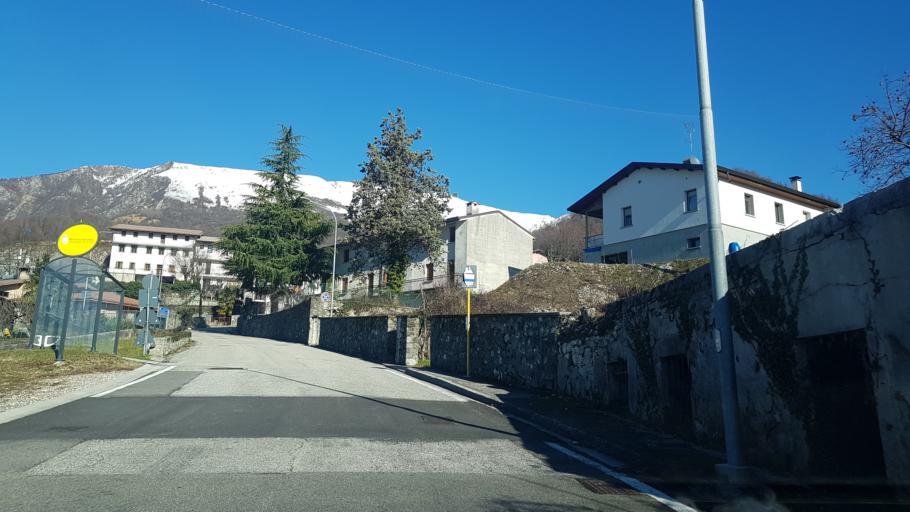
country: IT
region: Friuli Venezia Giulia
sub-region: Provincia di Udine
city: Montenars
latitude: 46.2524
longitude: 13.1673
